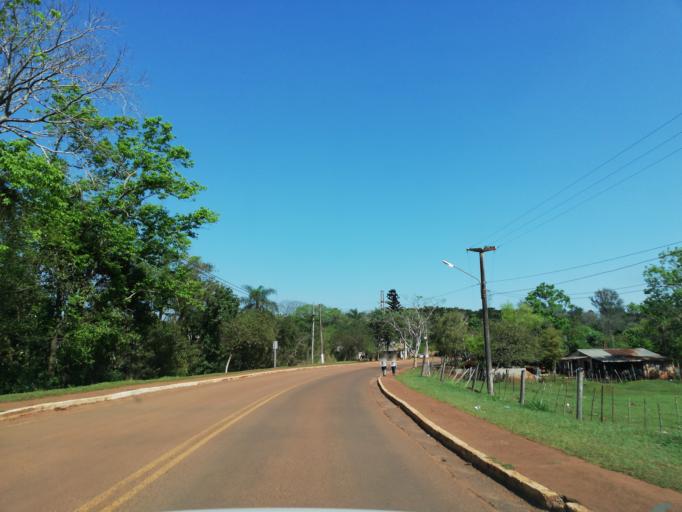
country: AR
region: Misiones
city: Puerto Eldorado
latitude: -26.4120
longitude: -54.6855
